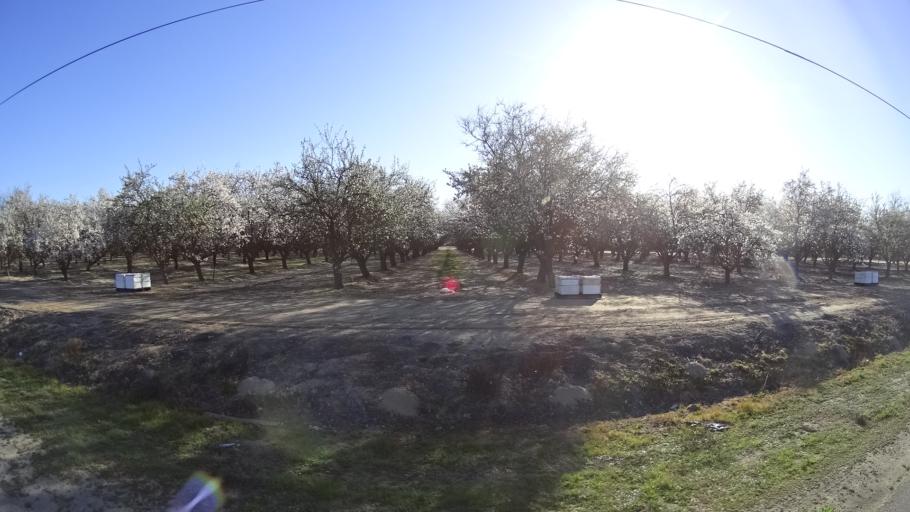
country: US
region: California
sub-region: Fresno County
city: Biola
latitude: 36.8019
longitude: -119.9164
